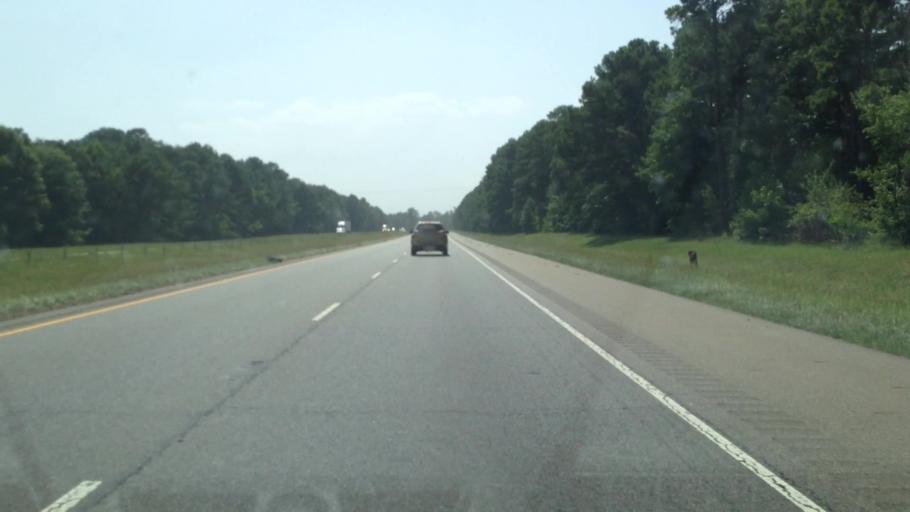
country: US
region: Louisiana
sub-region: Bossier Parish
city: Haughton
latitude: 32.5772
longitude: -93.4609
